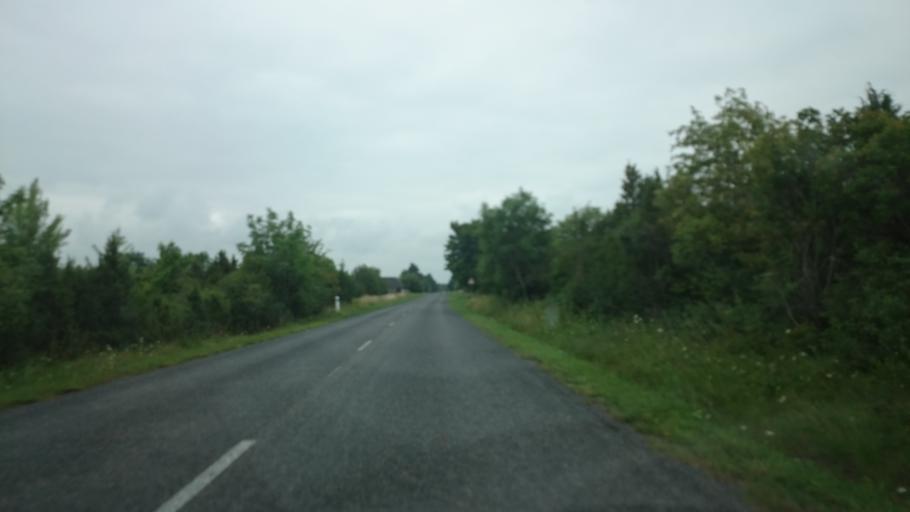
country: EE
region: Saare
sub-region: Orissaare vald
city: Orissaare
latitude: 58.5834
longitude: 23.0264
